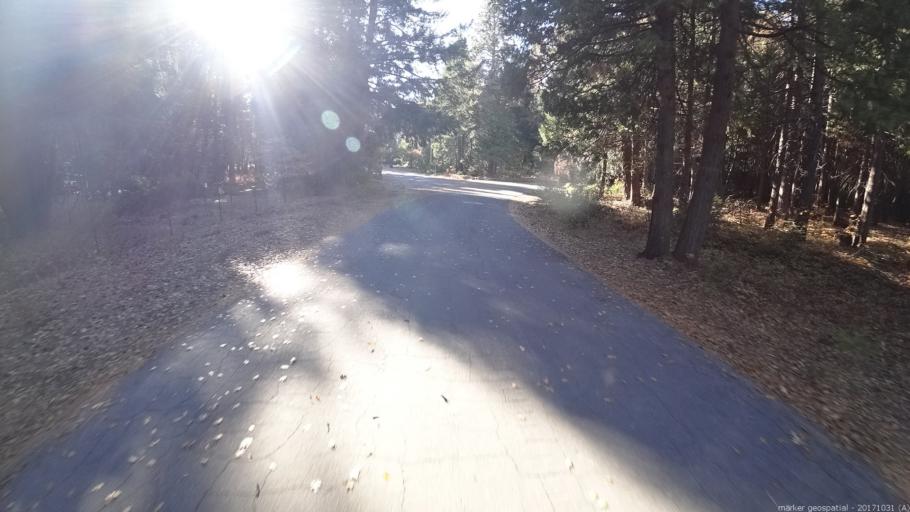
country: US
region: California
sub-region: Shasta County
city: Shingletown
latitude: 40.5254
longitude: -121.8358
